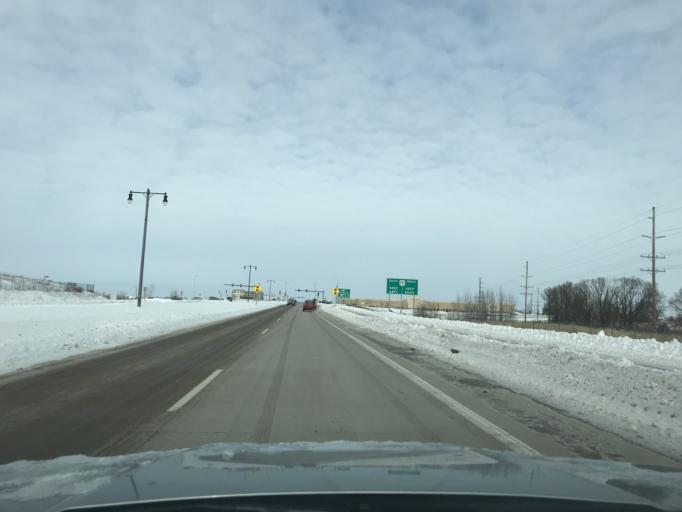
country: US
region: Wisconsin
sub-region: Dane County
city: Sun Prairie
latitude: 43.1585
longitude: -89.2657
